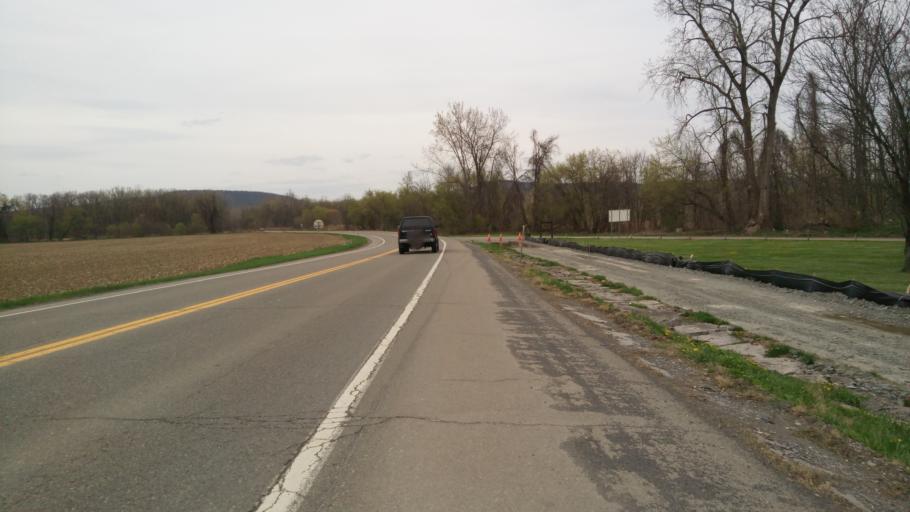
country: US
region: New York
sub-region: Chemung County
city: Southport
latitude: 42.0183
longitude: -76.7237
